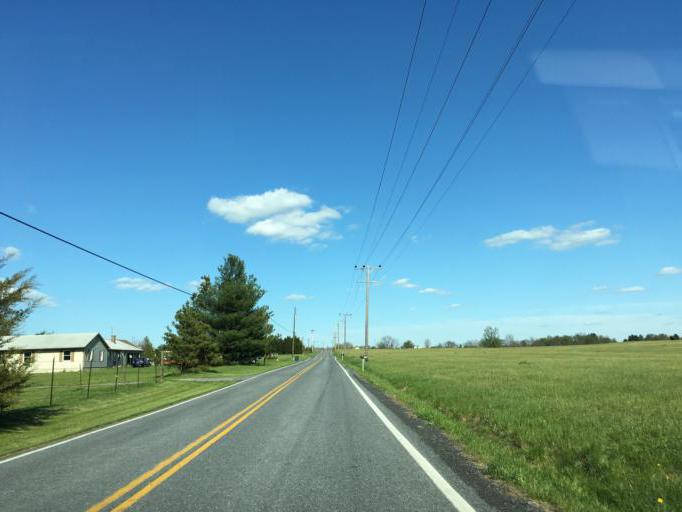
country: US
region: Maryland
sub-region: Frederick County
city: Thurmont
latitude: 39.6499
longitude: -77.3828
